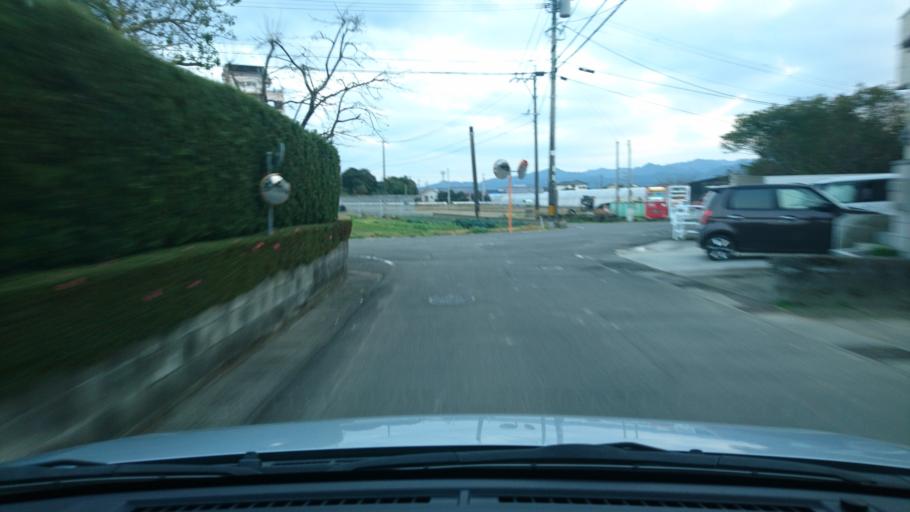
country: JP
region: Miyazaki
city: Miyazaki-shi
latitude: 31.8505
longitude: 131.4323
